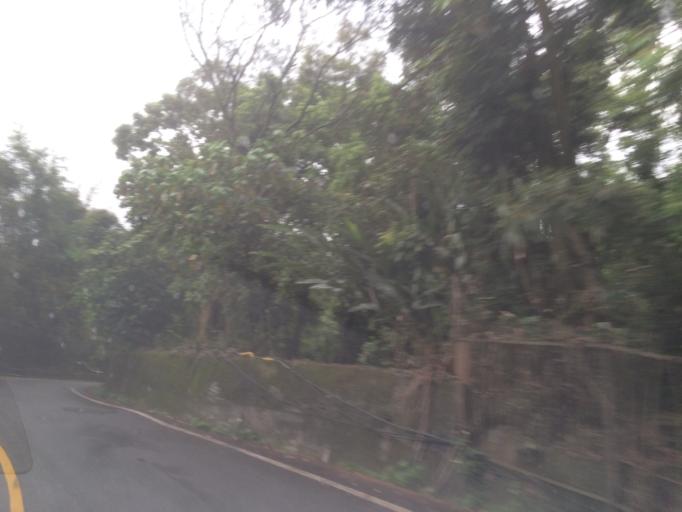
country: TW
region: Taiwan
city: Fengyuan
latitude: 24.1737
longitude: 120.8214
